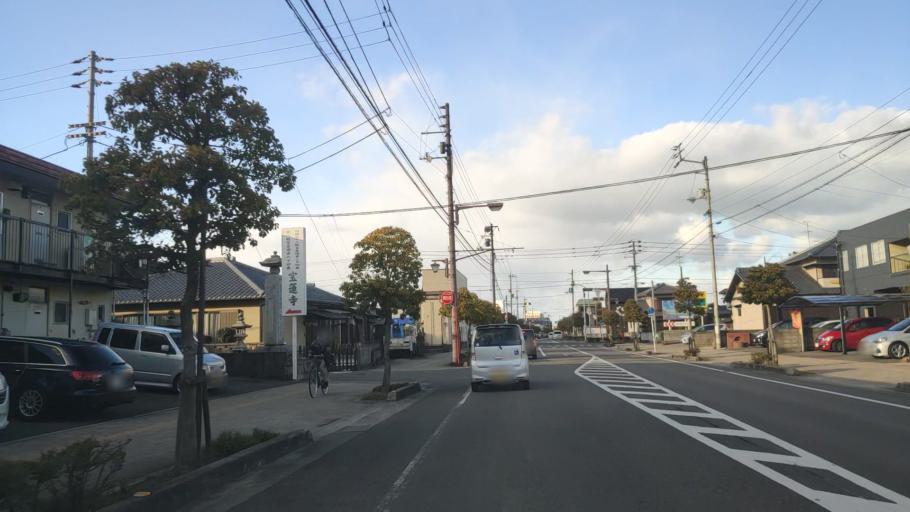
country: JP
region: Ehime
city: Saijo
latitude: 33.9203
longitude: 133.1849
